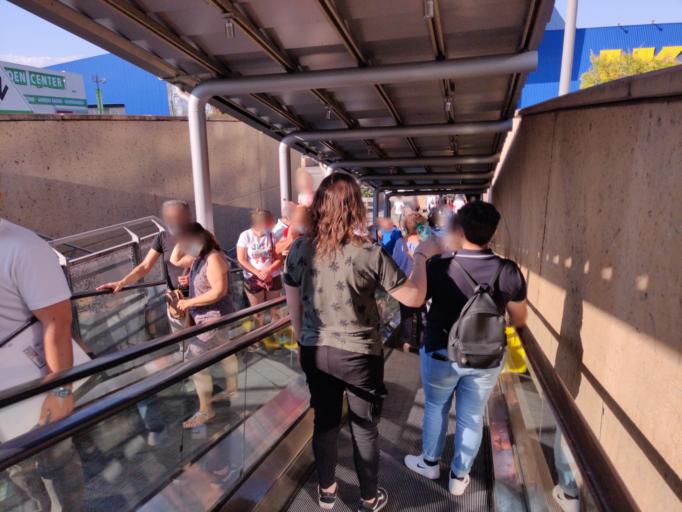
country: IT
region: Latium
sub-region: Citta metropolitana di Roma Capitale
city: Colle Verde
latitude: 41.9720
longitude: 12.5407
